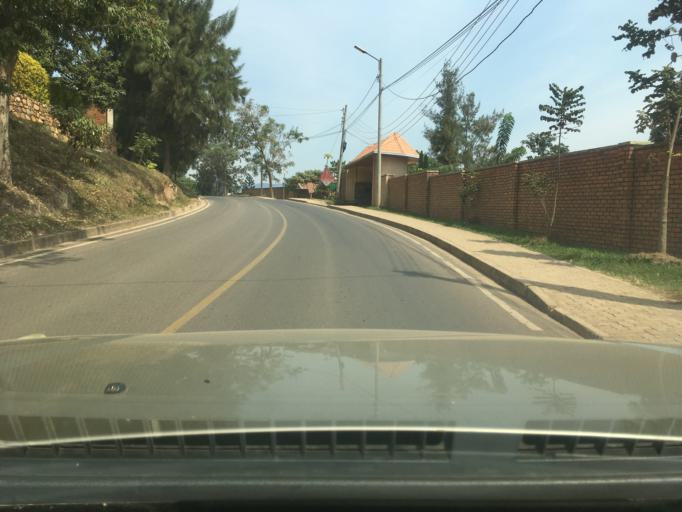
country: RW
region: Kigali
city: Kigali
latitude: -1.9620
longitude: 30.1034
